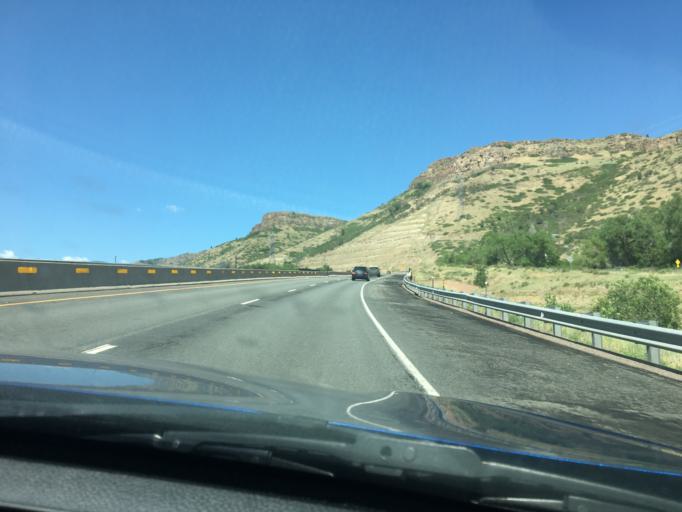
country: US
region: Colorado
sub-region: Jefferson County
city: Golden
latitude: 39.7691
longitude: -105.1979
